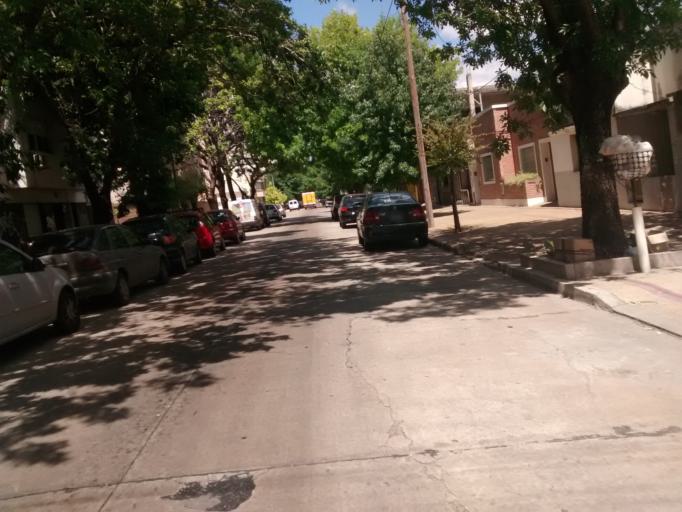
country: AR
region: Buenos Aires
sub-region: Partido de La Plata
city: La Plata
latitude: -34.9100
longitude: -57.9723
